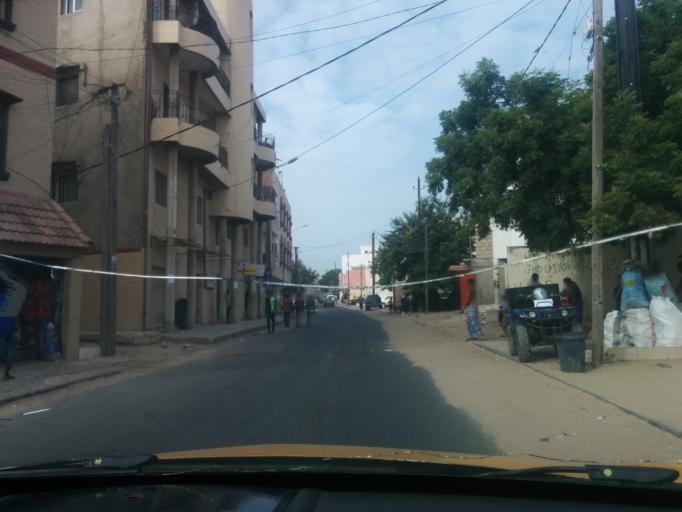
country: SN
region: Dakar
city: Grand Dakar
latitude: 14.7180
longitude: -17.4441
